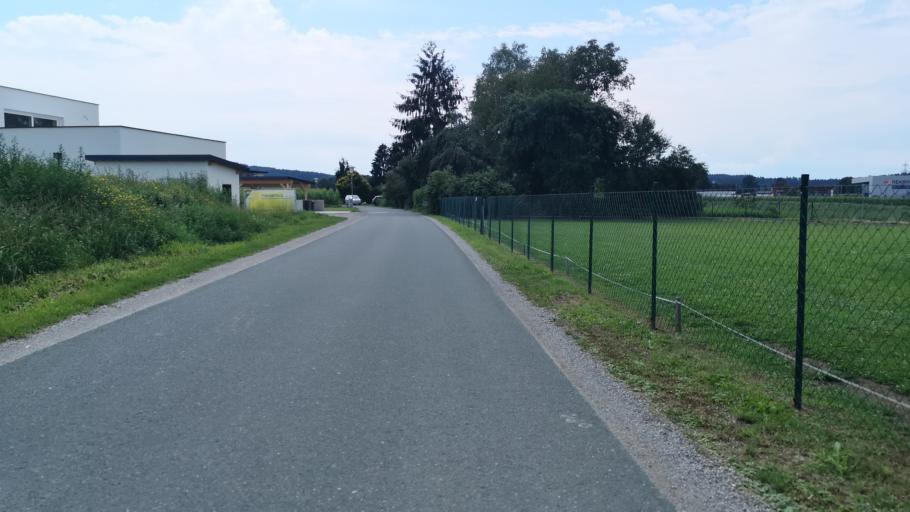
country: AT
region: Styria
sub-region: Politischer Bezirk Leibnitz
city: Weitendorf
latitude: 46.8960
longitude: 15.4765
